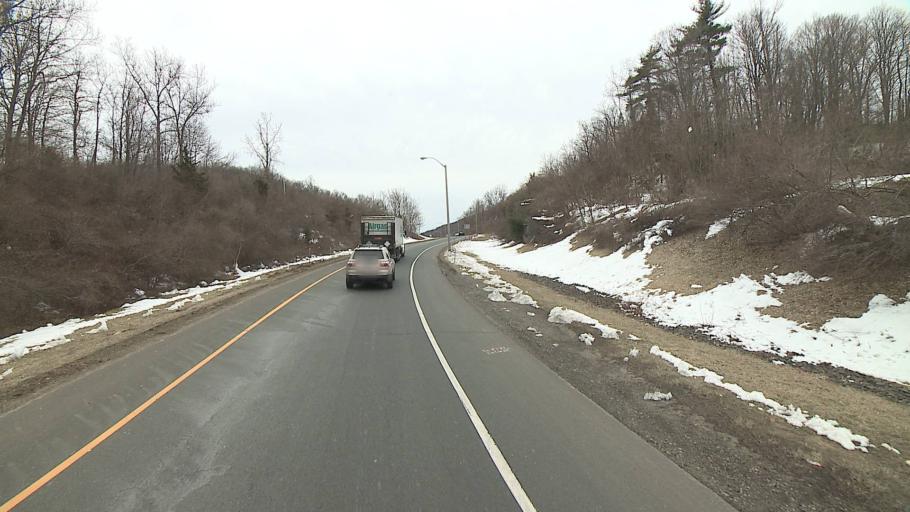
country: US
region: Connecticut
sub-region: Fairfield County
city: Danbury
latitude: 41.3700
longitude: -73.4750
